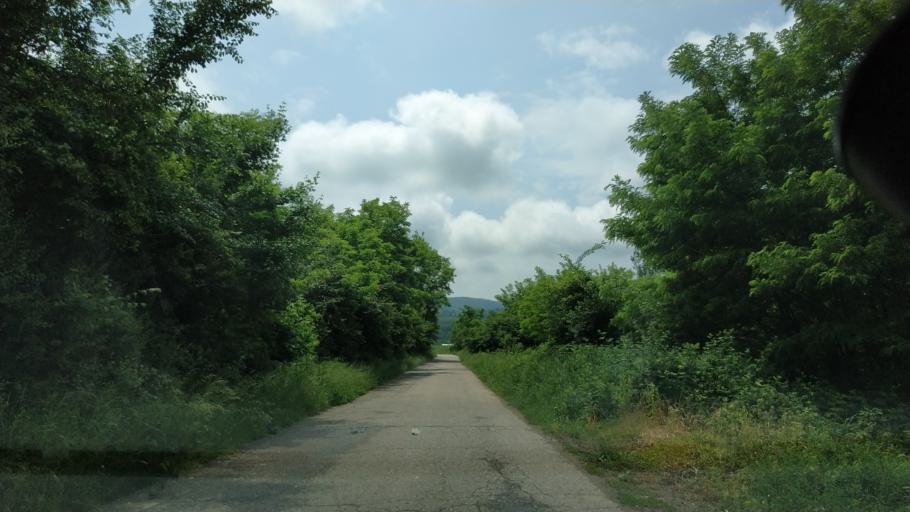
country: RS
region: Central Serbia
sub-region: Nisavski Okrug
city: Aleksinac
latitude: 43.4343
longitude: 21.7116
